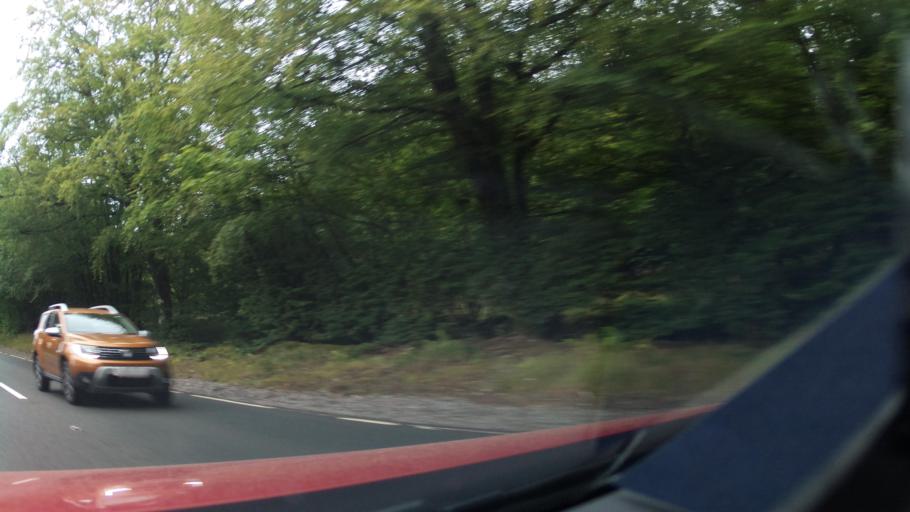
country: GB
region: Scotland
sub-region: Dumfries and Galloway
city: Moffat
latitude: 55.2430
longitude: -3.4613
